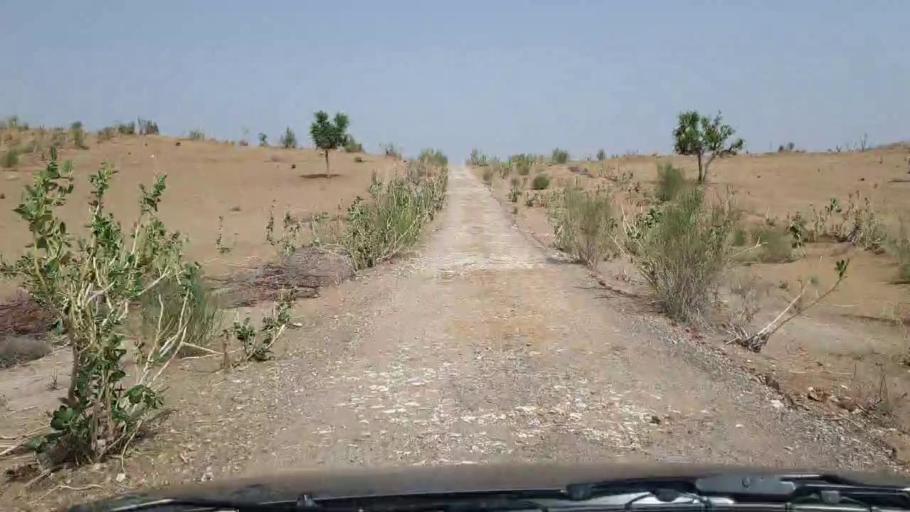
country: PK
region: Sindh
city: Chor
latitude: 25.4689
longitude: 70.5218
